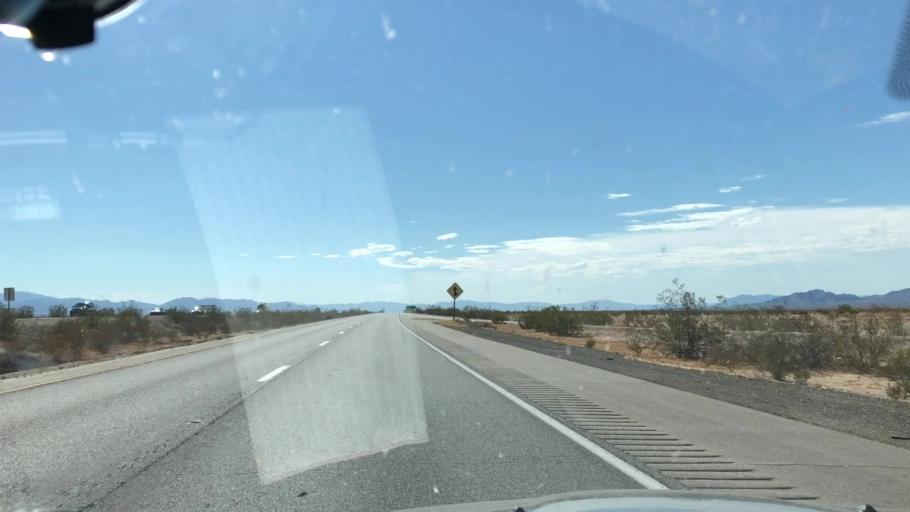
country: US
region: California
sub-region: Riverside County
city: Mesa Verde
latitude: 33.6081
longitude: -114.9915
